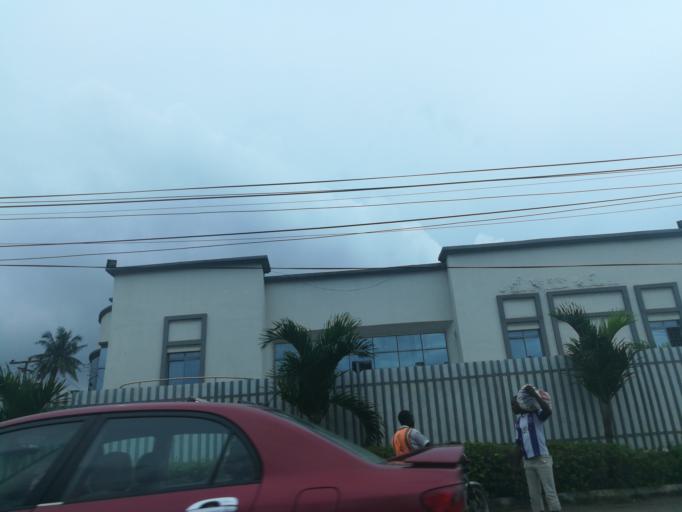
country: NG
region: Lagos
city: Ikeja
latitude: 6.6088
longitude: 3.3431
